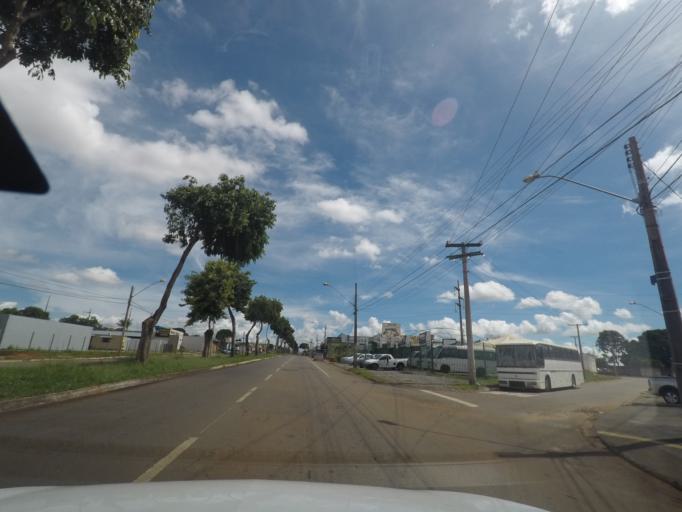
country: BR
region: Goias
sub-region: Goiania
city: Goiania
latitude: -16.7346
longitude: -49.3264
